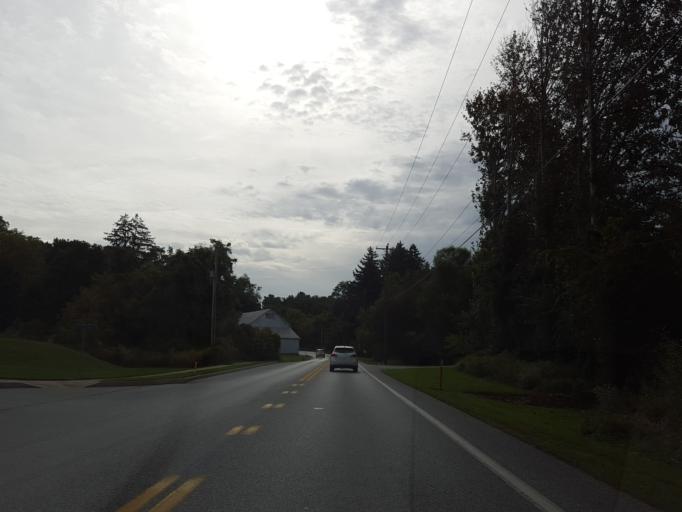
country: US
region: Pennsylvania
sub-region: York County
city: Yoe
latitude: 39.9033
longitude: -76.6244
